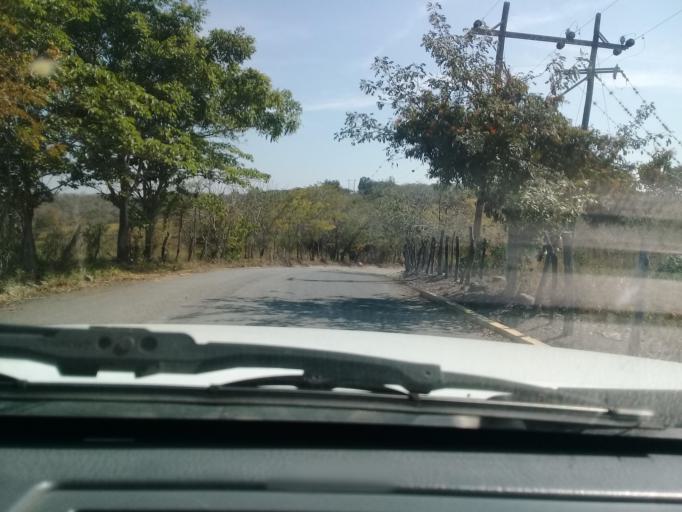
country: MX
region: Veracruz
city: Actopan
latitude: 19.4777
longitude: -96.6426
